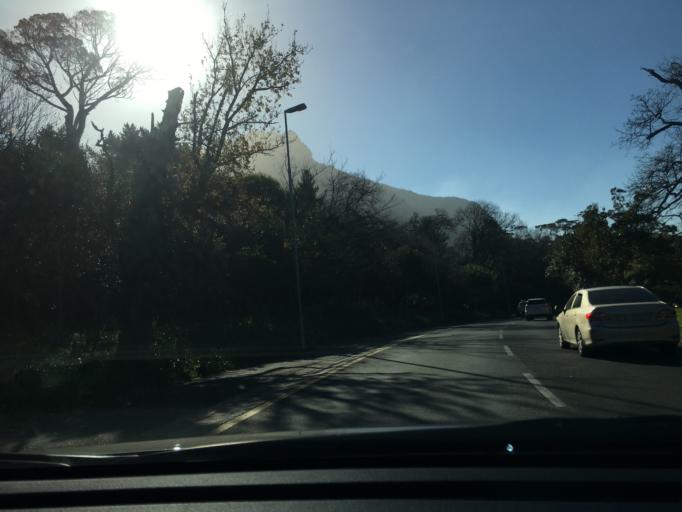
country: ZA
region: Western Cape
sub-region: City of Cape Town
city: Newlands
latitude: -33.9750
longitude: 18.4476
